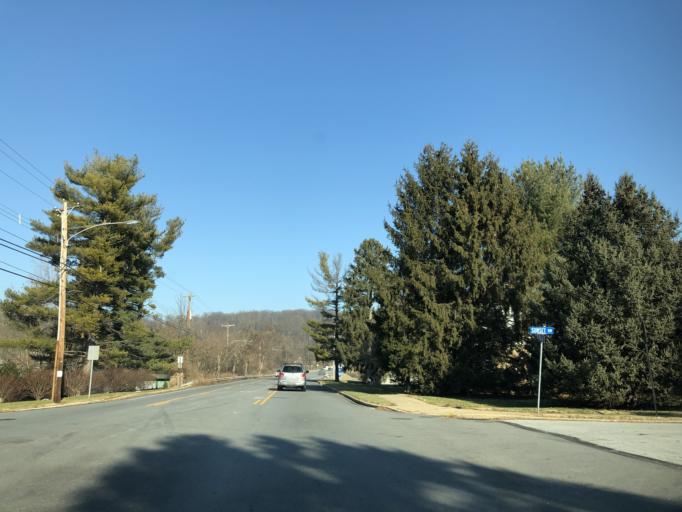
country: US
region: Pennsylvania
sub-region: Chester County
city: Downingtown
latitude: 40.0153
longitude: -75.6953
